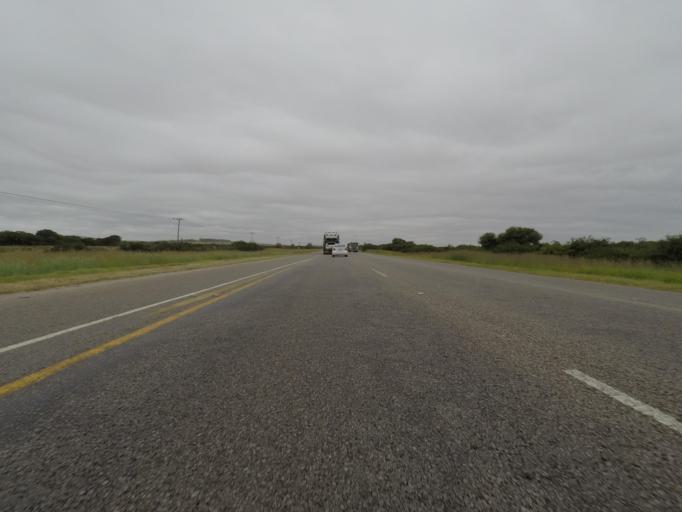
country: ZA
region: Eastern Cape
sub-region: Nelson Mandela Bay Metropolitan Municipality
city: Port Elizabeth
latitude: -33.6532
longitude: 25.8685
